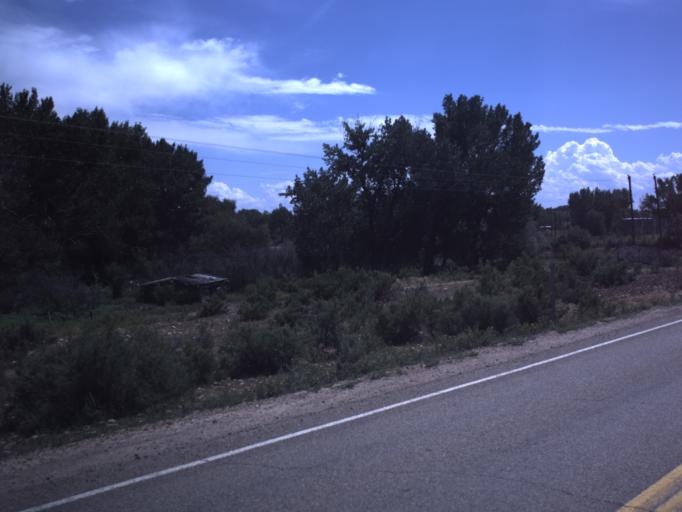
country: US
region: Utah
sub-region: Duchesne County
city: Roosevelt
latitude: 40.0870
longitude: -109.6764
